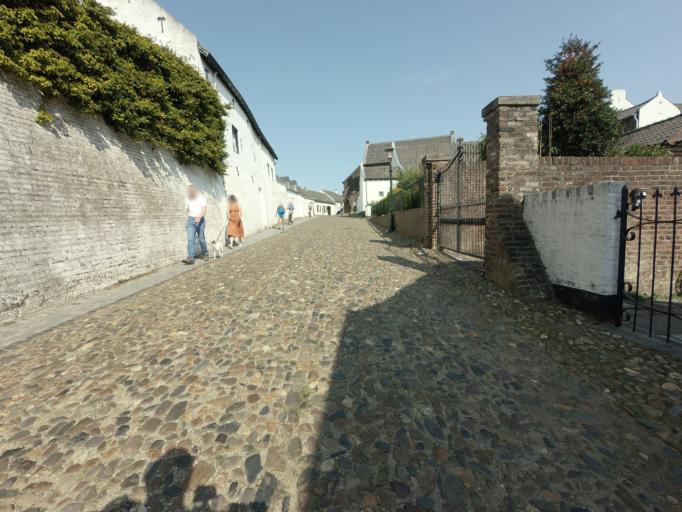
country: NL
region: Limburg
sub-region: Gemeente Maasgouw
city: Maasbracht
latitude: 51.1604
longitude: 5.8390
